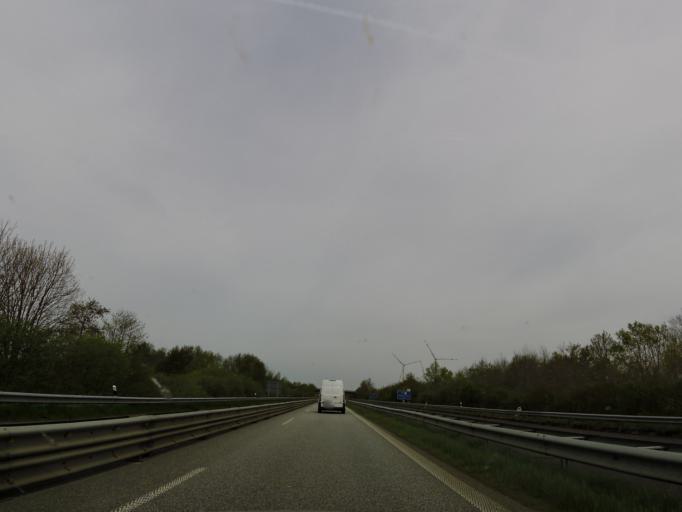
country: DE
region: Schleswig-Holstein
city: Tensbuttel-Rost
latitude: 54.1245
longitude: 9.2563
